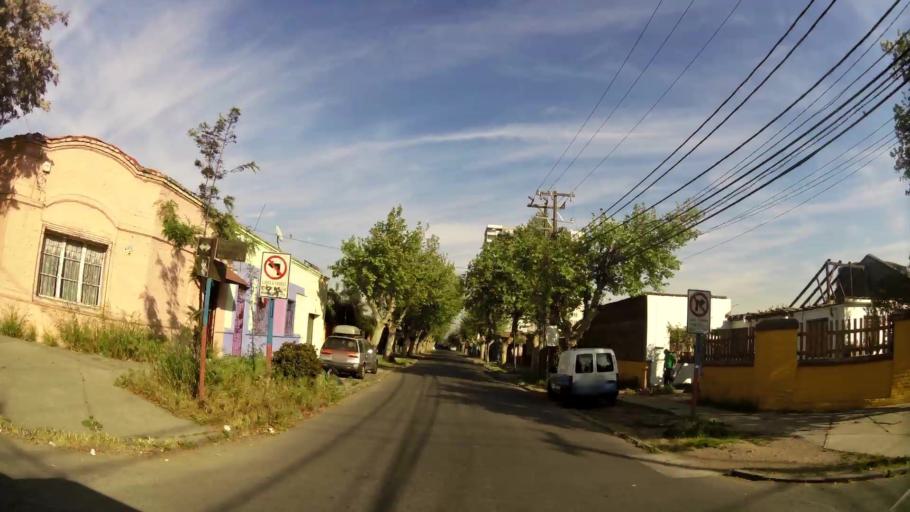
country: CL
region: Santiago Metropolitan
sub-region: Provincia de Santiago
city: Santiago
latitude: -33.5098
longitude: -70.6638
